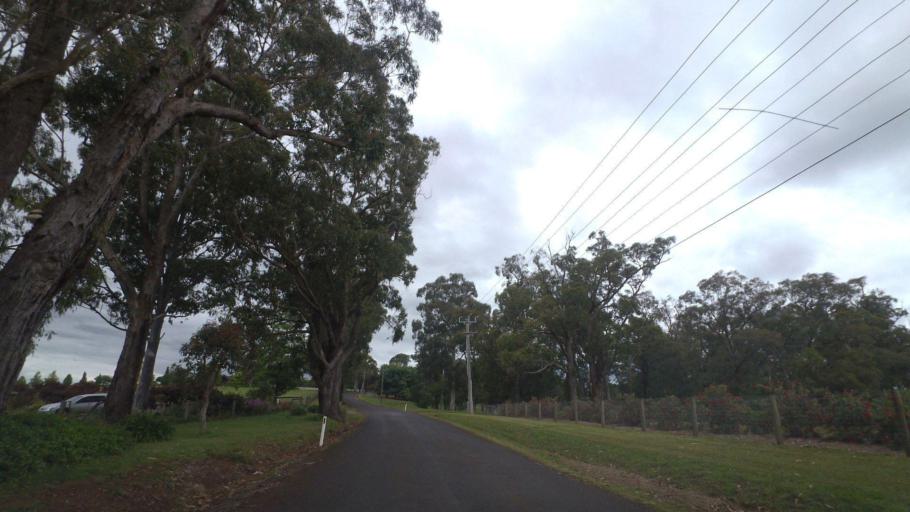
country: AU
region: Victoria
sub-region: Yarra Ranges
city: Mount Evelyn
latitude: -37.7894
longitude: 145.4211
